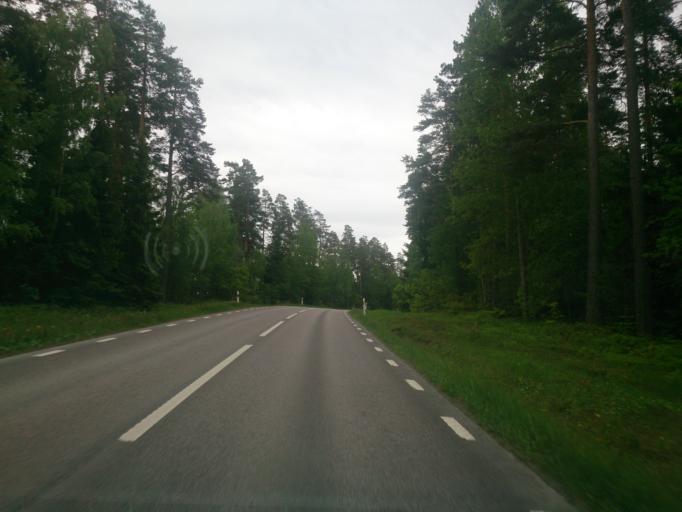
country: SE
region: OEstergoetland
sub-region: Atvidabergs Kommun
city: Atvidaberg
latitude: 58.2665
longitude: 15.9248
